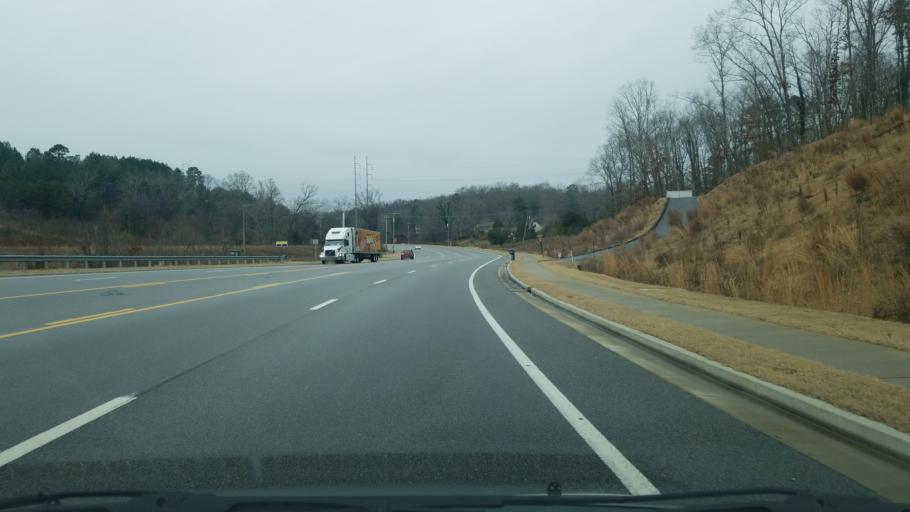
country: US
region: Tennessee
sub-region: Hamilton County
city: Collegedale
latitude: 35.0647
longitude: -85.0802
